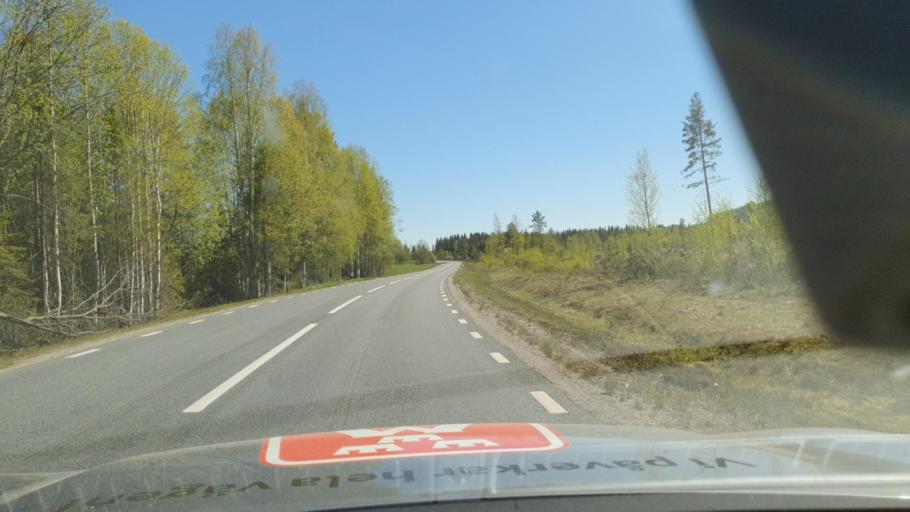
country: SE
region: Vaesternorrland
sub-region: OErnskoeldsviks Kommun
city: Bredbyn
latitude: 63.7485
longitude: 18.4951
